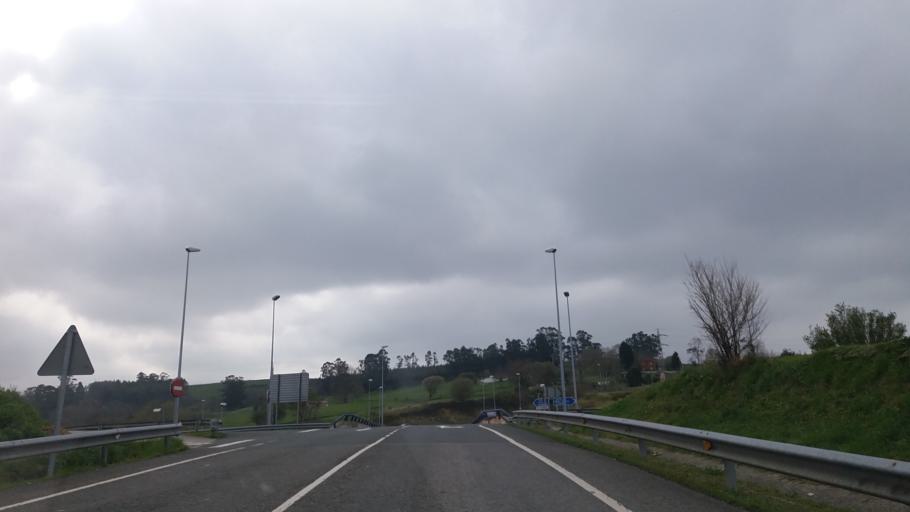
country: ES
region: Cantabria
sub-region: Provincia de Cantabria
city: Reocin
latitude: 43.3462
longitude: -4.1363
